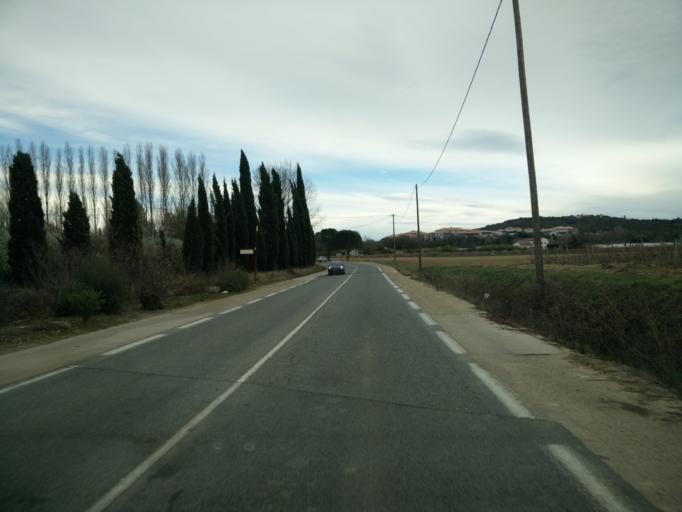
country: FR
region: Provence-Alpes-Cote d'Azur
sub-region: Departement du Var
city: Puget-sur-Argens
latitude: 43.4332
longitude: 6.6634
